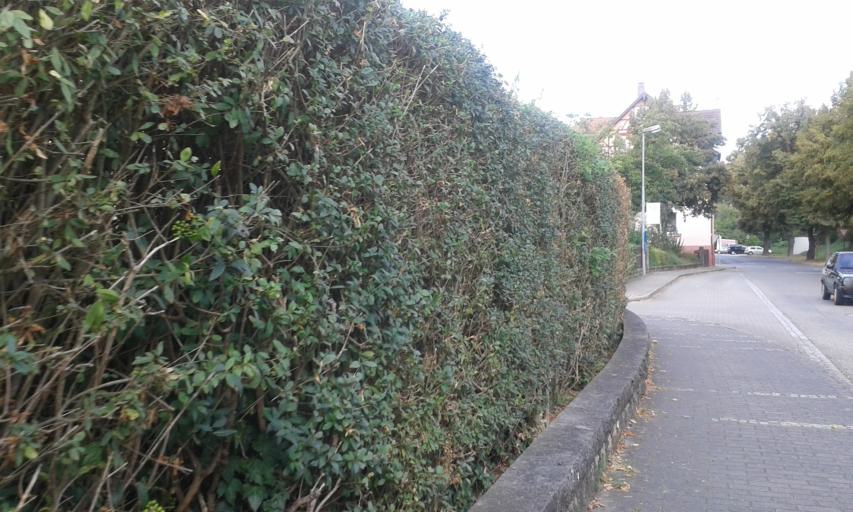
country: DE
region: Baden-Wuerttemberg
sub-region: Regierungsbezirk Stuttgart
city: Lauda-Konigshofen
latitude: 49.5703
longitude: 9.7050
